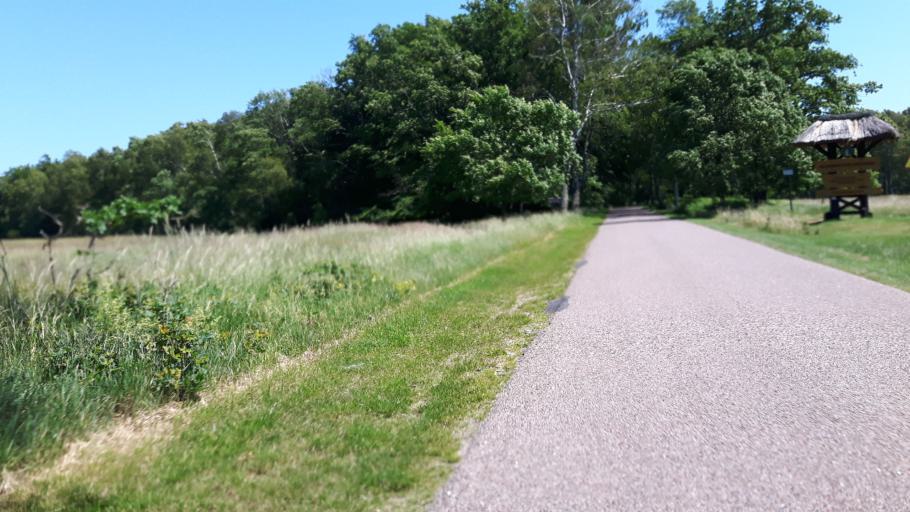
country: PL
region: Pomeranian Voivodeship
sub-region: Powiat slupski
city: Smoldzino
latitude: 54.6864
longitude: 17.2930
